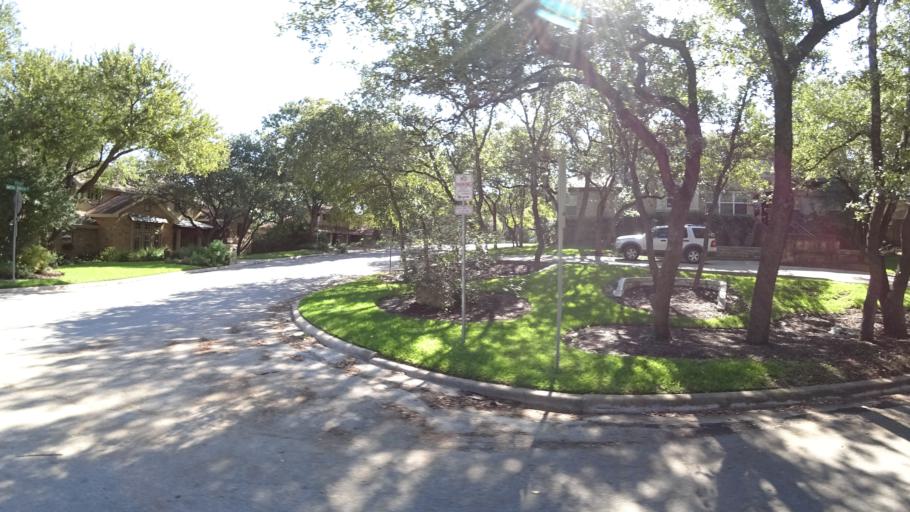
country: US
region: Texas
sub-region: Travis County
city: Rollingwood
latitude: 30.2748
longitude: -97.8100
